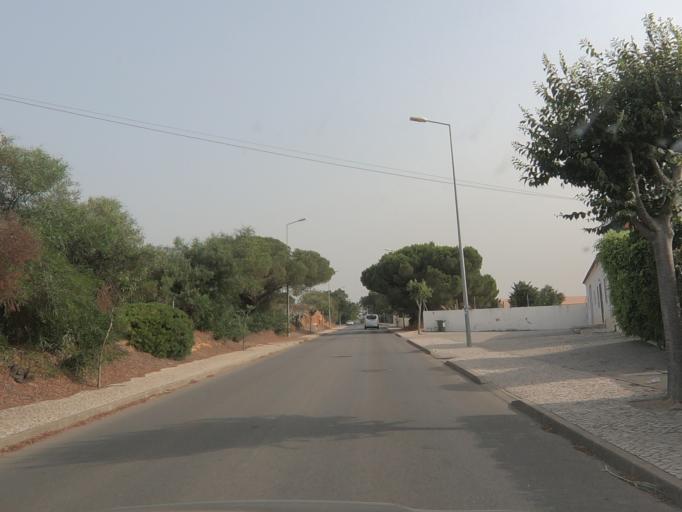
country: PT
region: Faro
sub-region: Albufeira
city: Guia
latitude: 37.0895
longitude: -8.3103
